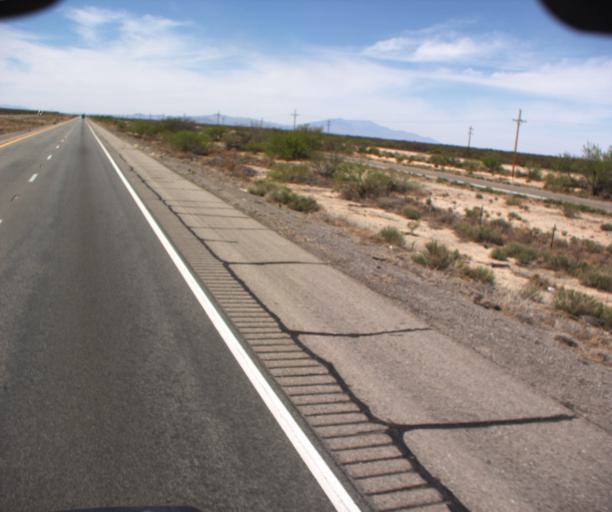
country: US
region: Arizona
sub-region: Cochise County
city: Willcox
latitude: 32.2889
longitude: -109.3163
